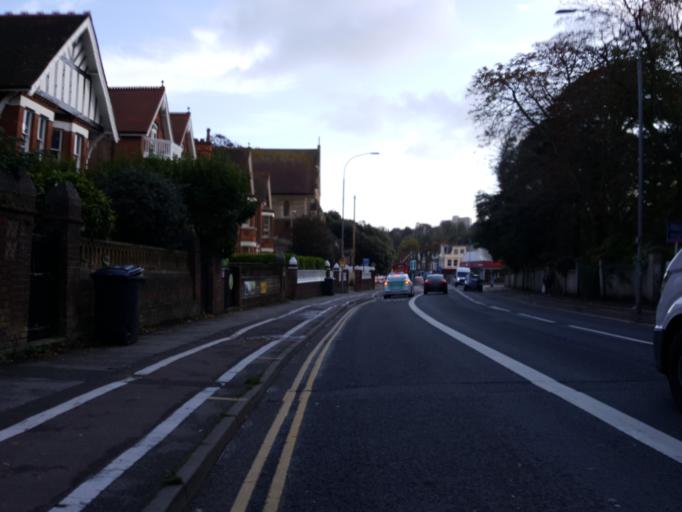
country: GB
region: England
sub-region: Brighton and Hove
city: Brighton
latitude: 50.8453
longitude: -0.1513
